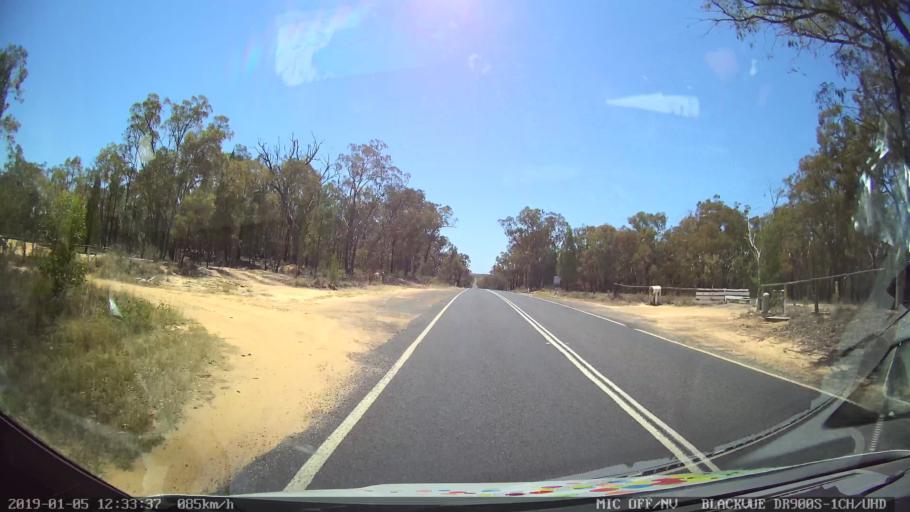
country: AU
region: New South Wales
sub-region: Warrumbungle Shire
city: Coonabarabran
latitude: -31.2142
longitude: 149.3977
